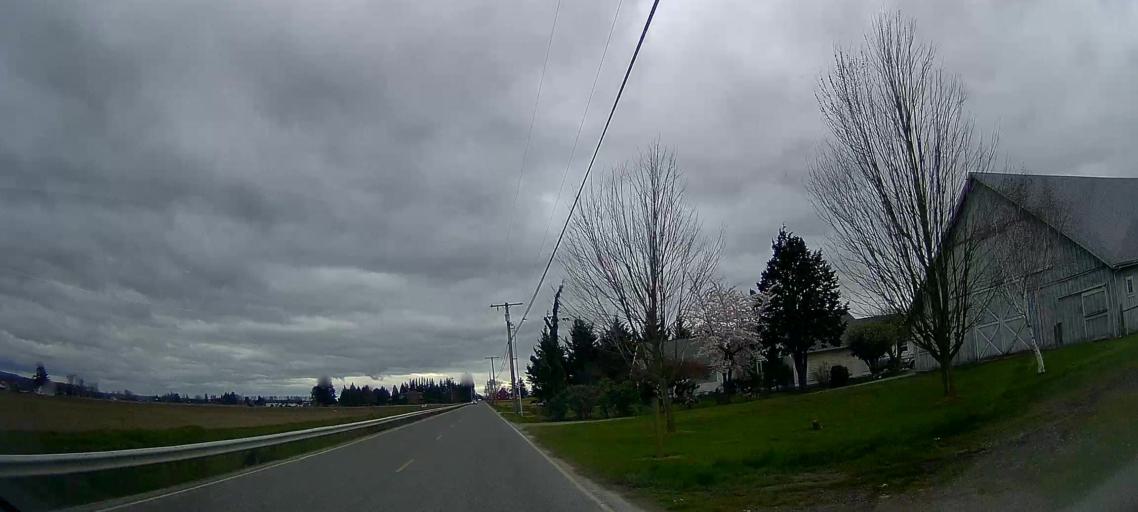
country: US
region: Washington
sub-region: Skagit County
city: Mount Vernon
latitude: 48.4100
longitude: -122.4011
